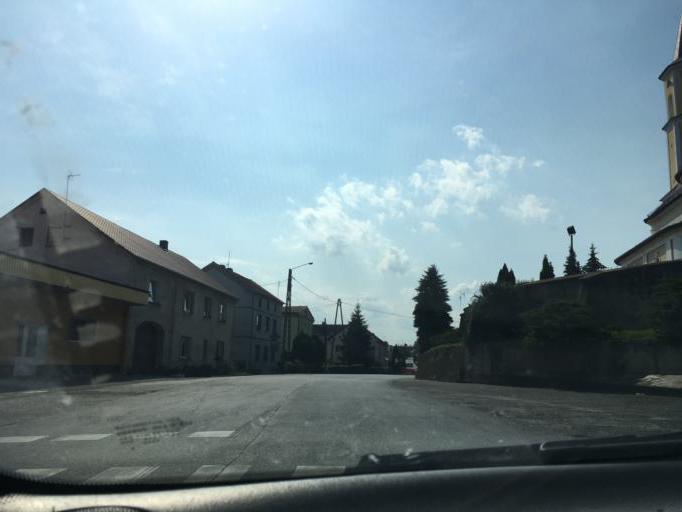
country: PL
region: Opole Voivodeship
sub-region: Powiat prudnicki
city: Raclawice Slaskie
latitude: 50.3120
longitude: 17.7753
